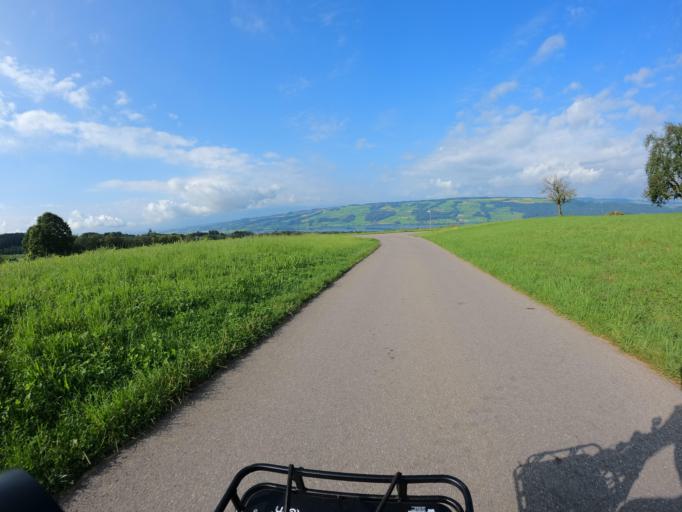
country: CH
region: Lucerne
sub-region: Hochdorf District
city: Hitzkirch
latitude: 47.2238
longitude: 8.2913
